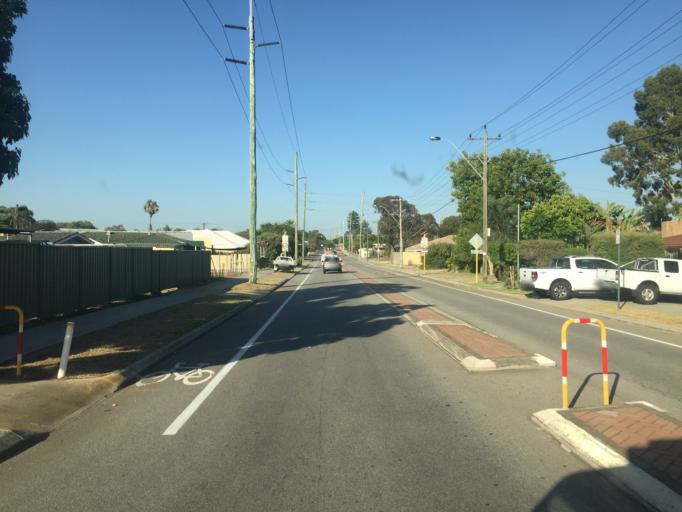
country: AU
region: Western Australia
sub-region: Belmont
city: Belmont
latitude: -31.9564
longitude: 115.9337
